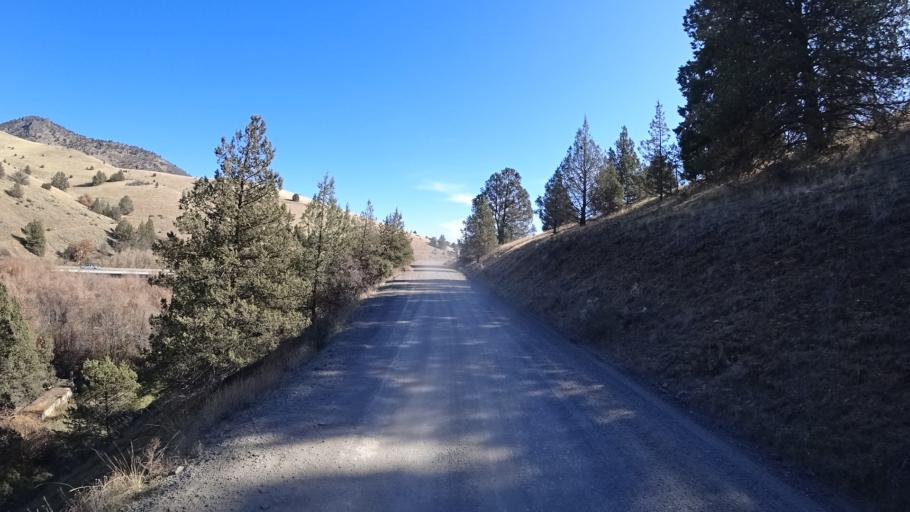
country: US
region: California
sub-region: Siskiyou County
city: Yreka
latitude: 41.7807
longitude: -122.5979
